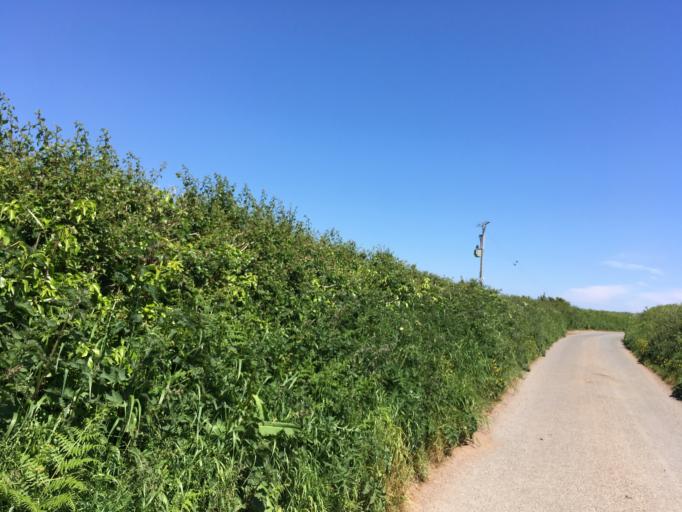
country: GB
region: England
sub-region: Devon
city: Dartmouth
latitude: 50.3505
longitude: -3.5393
